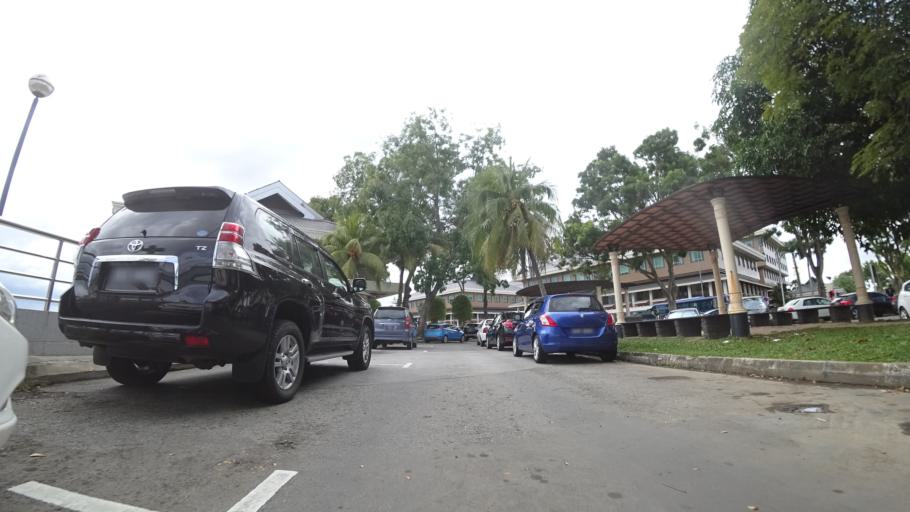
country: BN
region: Brunei and Muara
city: Bandar Seri Begawan
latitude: 4.8868
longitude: 114.9420
